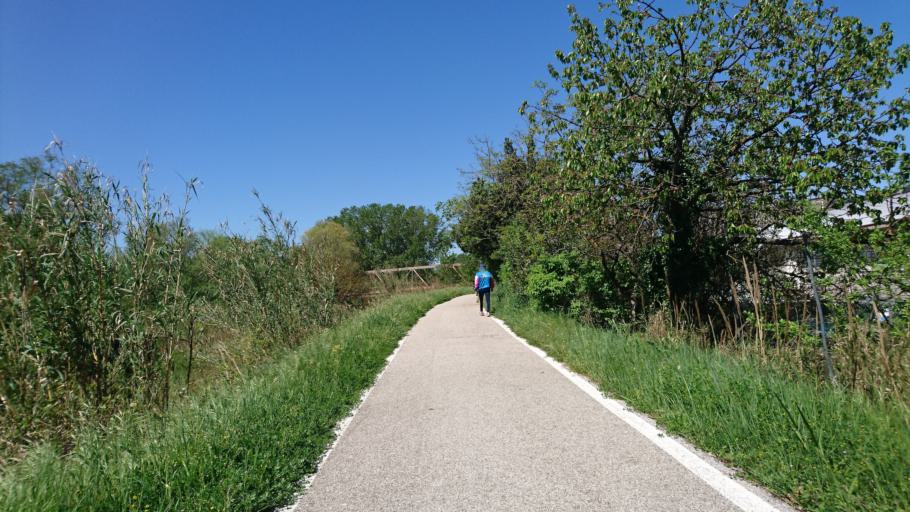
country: IT
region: The Marches
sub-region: Provincia di Pesaro e Urbino
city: Pesaro
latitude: 43.9015
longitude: 12.8851
